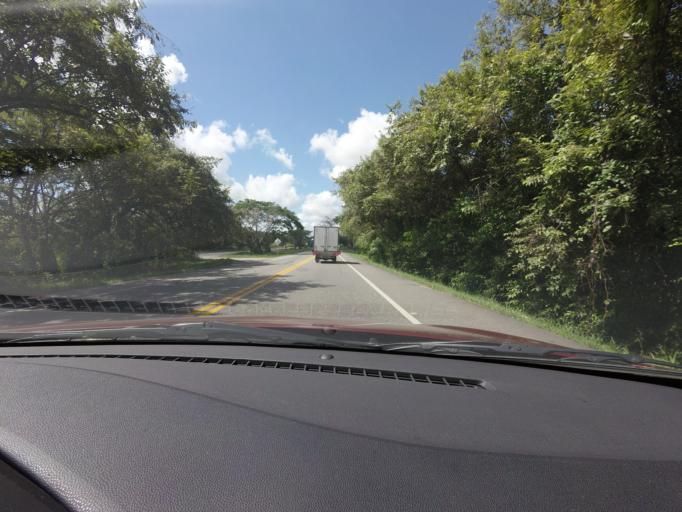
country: CO
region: Tolima
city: Saldana
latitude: 3.9408
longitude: -75.0139
